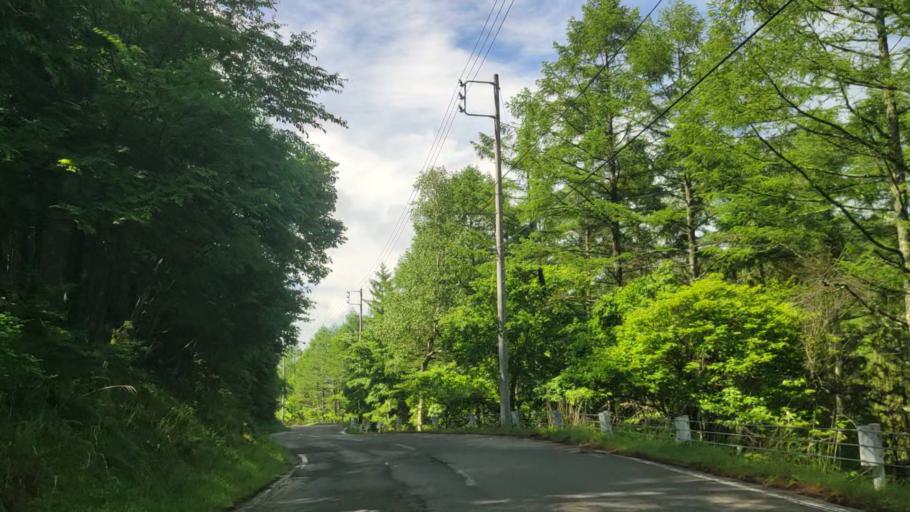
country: JP
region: Nagano
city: Suwa
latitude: 36.0992
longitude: 138.1417
